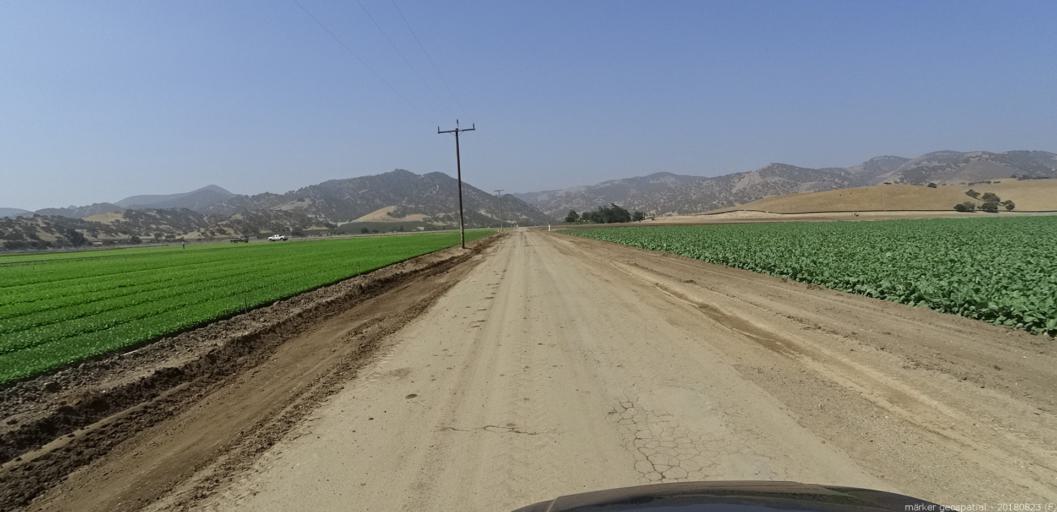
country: US
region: California
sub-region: Monterey County
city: King City
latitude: 36.2296
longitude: -121.1800
